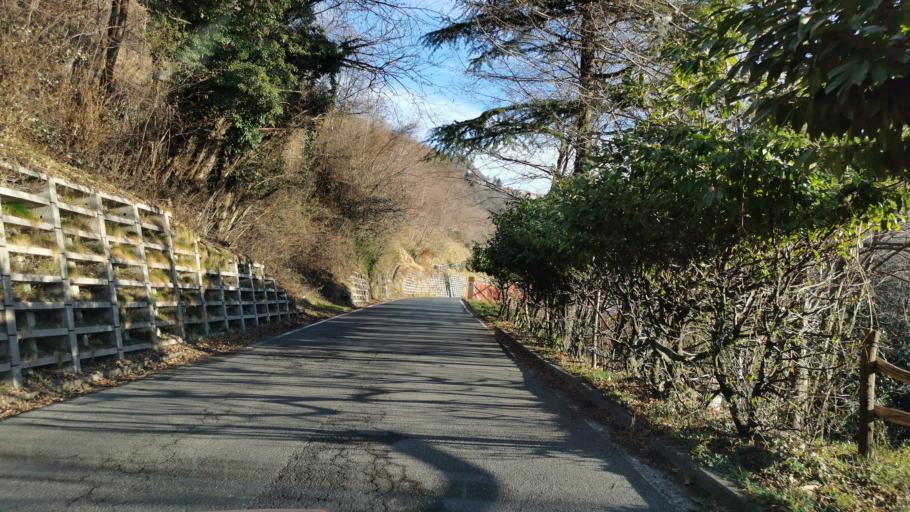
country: IT
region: Lombardy
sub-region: Provincia di Como
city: Plesio
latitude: 46.0438
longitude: 9.2257
